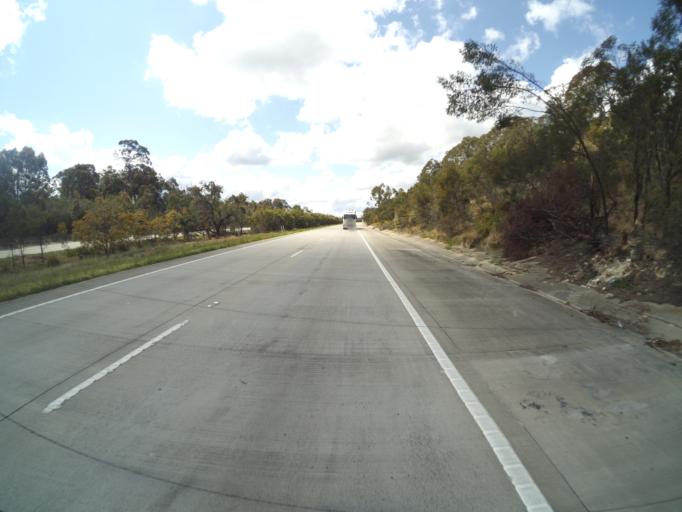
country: AU
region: New South Wales
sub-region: Wingecarribee
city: Bowral
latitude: -34.4487
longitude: 150.3773
